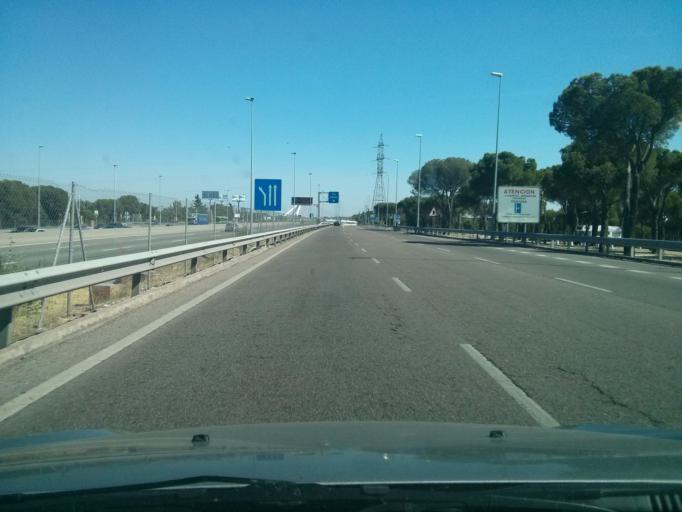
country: ES
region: Madrid
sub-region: Provincia de Madrid
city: Las Rozas de Madrid
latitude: 40.5161
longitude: -3.8842
